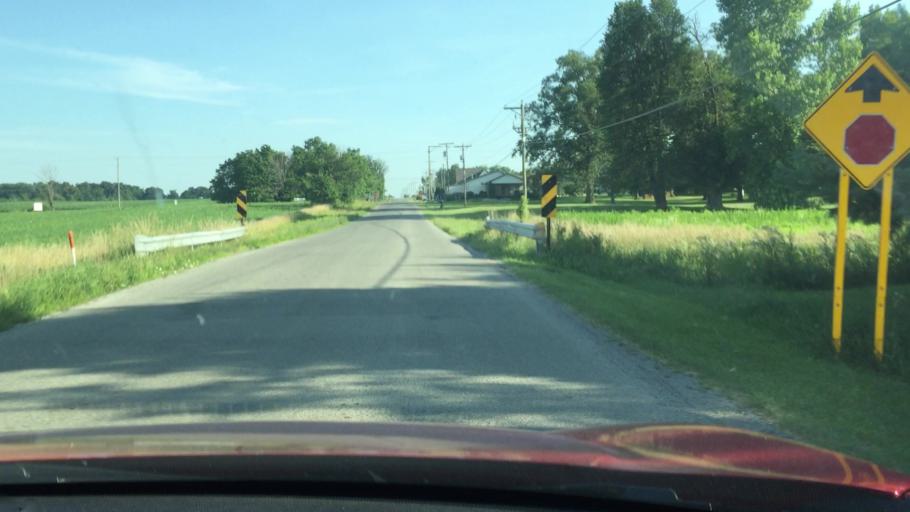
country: US
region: Ohio
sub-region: Hardin County
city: Ada
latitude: 40.7347
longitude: -83.8424
